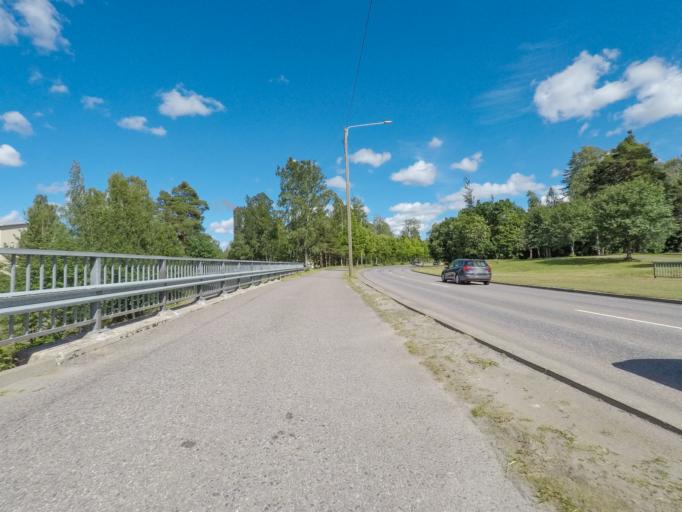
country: FI
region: South Karelia
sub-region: Lappeenranta
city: Lappeenranta
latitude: 61.0630
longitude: 28.2287
